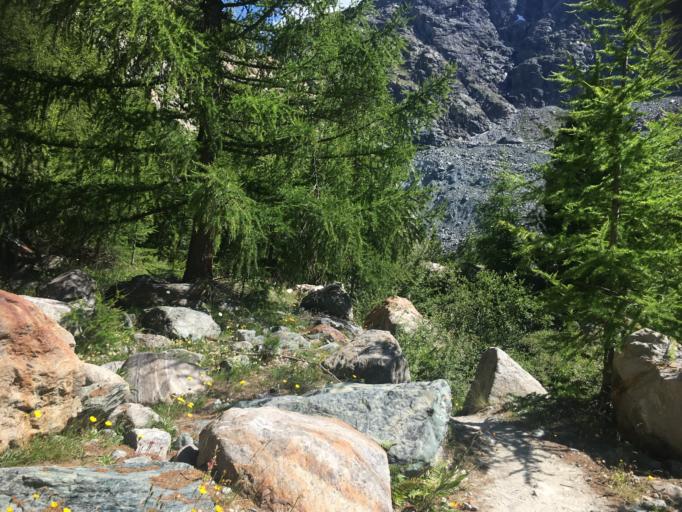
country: CH
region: Valais
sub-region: Visp District
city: Zermatt
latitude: 45.9900
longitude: 7.7355
